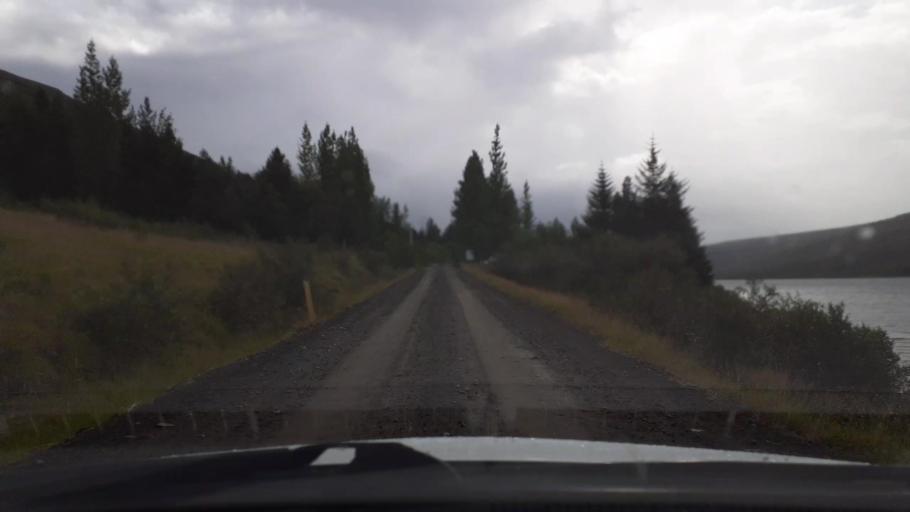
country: IS
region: Capital Region
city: Mosfellsbaer
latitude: 64.4977
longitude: -21.3593
